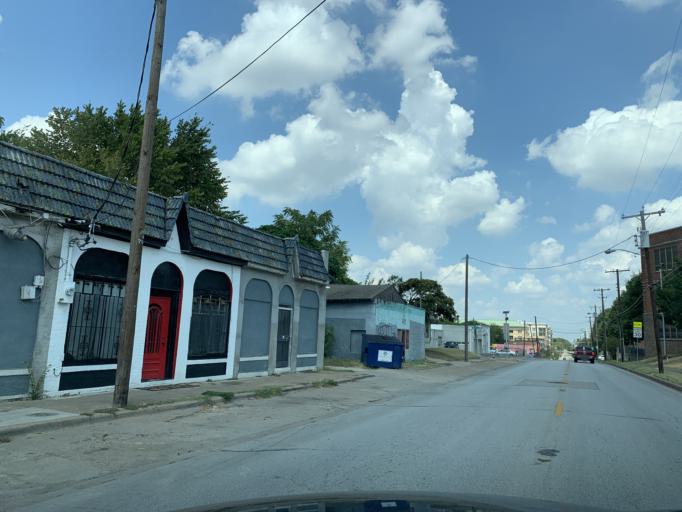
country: US
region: Texas
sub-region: Dallas County
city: Dallas
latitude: 32.7465
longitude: -96.8228
